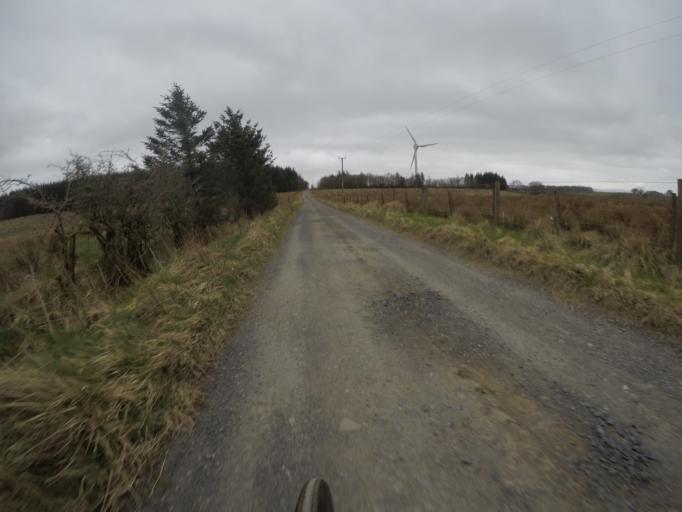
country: GB
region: Scotland
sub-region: East Ayrshire
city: Newmilns
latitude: 55.6293
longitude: -4.3421
